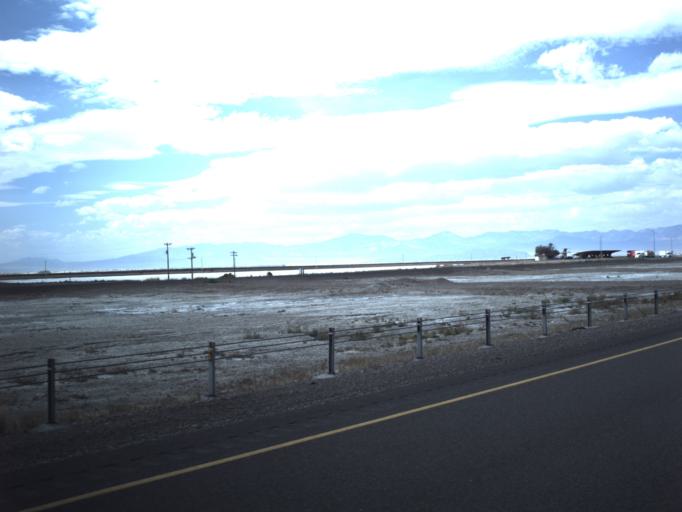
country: US
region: Utah
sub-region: Tooele County
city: Wendover
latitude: 40.7394
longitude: -113.8505
